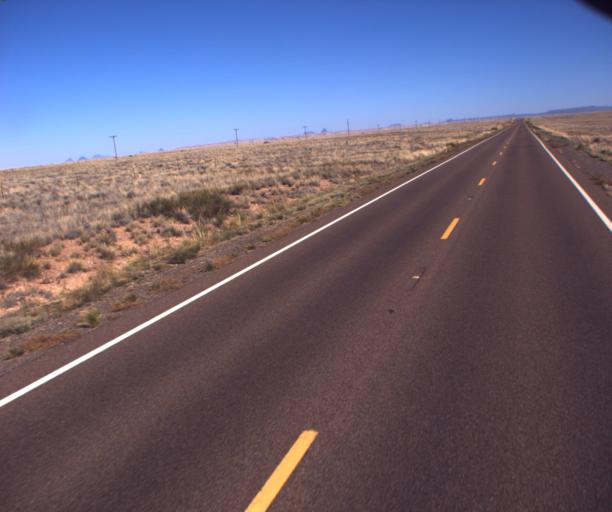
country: US
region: Arizona
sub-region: Navajo County
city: Winslow
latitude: 35.0897
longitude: -110.5479
